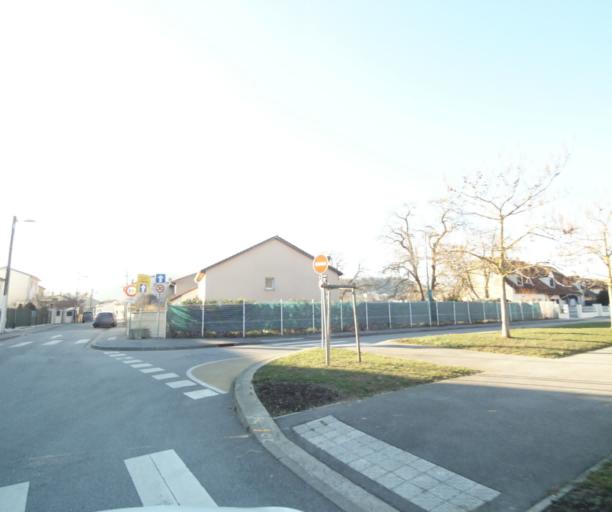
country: FR
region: Lorraine
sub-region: Departement de Meurthe-et-Moselle
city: Malzeville
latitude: 48.7141
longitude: 6.1810
